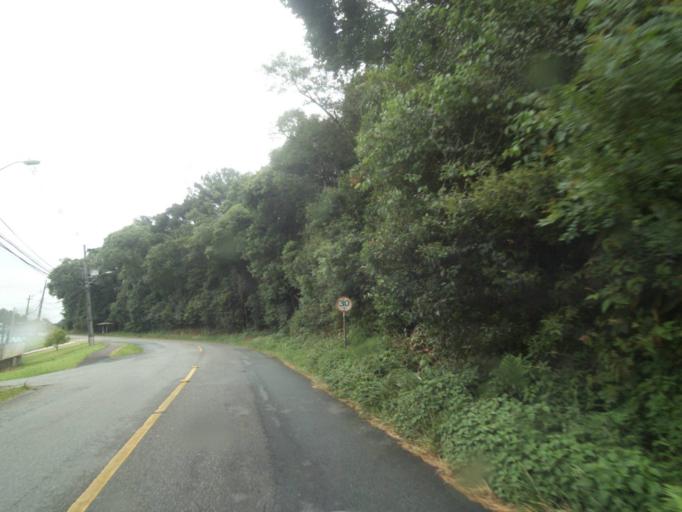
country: BR
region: Parana
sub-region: Curitiba
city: Curitiba
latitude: -25.4272
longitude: -49.3282
